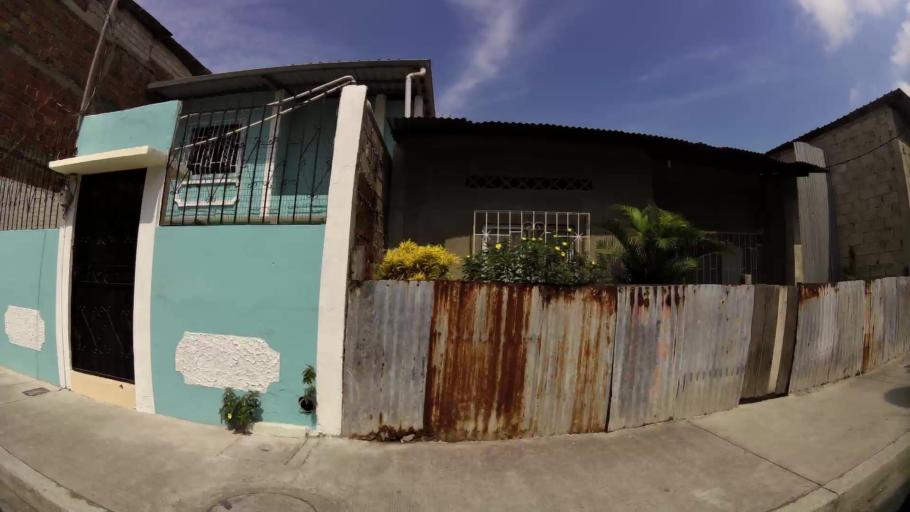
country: EC
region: Guayas
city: Guayaquil
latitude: -2.2762
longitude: -79.8870
